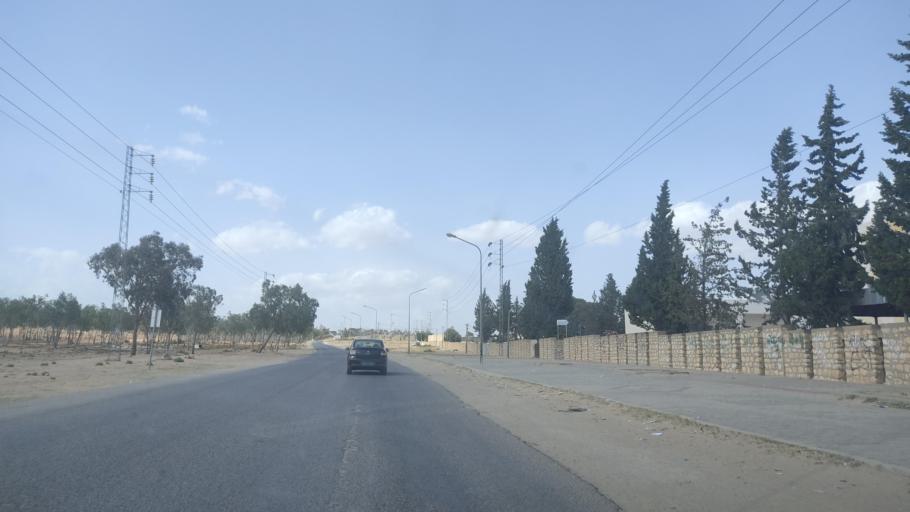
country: TN
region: Sidi Bu Zayd
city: Sidi Bouzid
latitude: 35.1052
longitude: 9.5371
